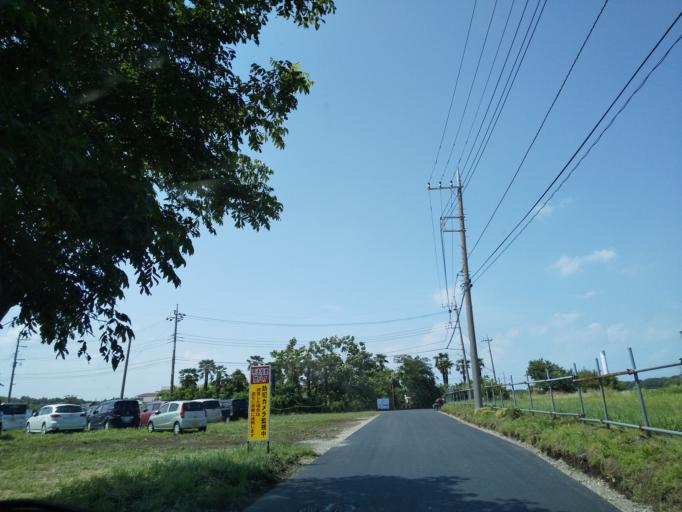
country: JP
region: Kanagawa
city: Zama
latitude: 35.5194
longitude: 139.3890
